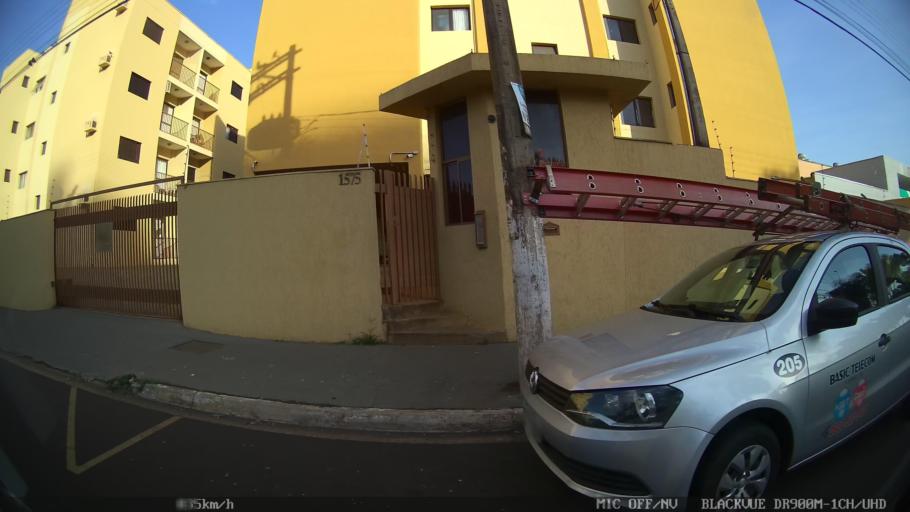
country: BR
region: Sao Paulo
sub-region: Ribeirao Preto
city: Ribeirao Preto
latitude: -21.1667
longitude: -47.8290
